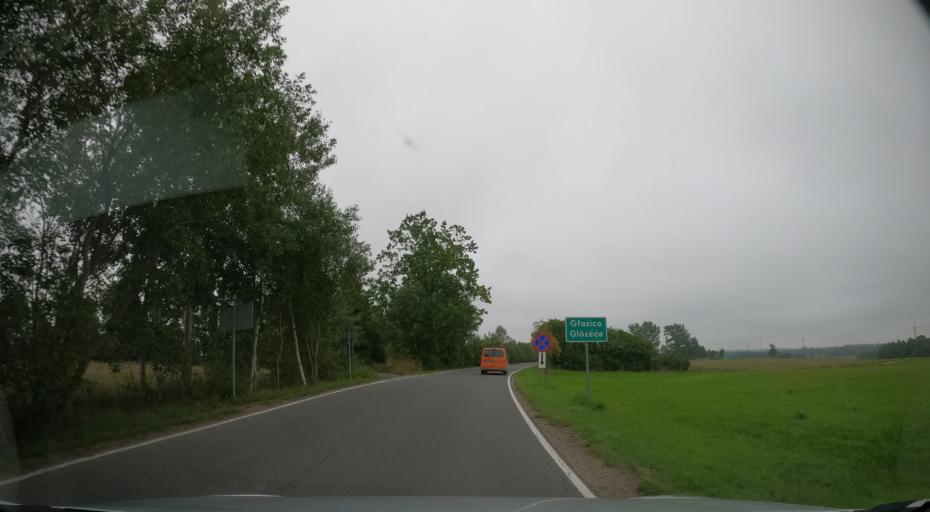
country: PL
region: Pomeranian Voivodeship
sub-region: Powiat wejherowski
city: Szemud
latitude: 54.5000
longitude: 18.1770
